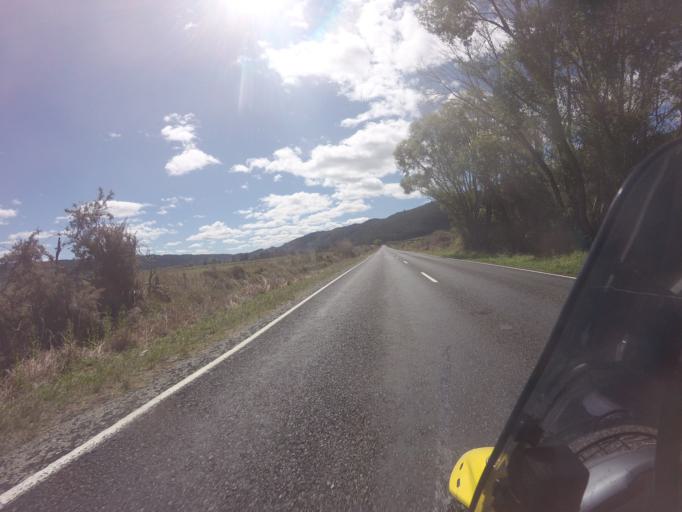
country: NZ
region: Bay of Plenty
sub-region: Kawerau District
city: Kawerau
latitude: -38.2167
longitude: 176.8433
